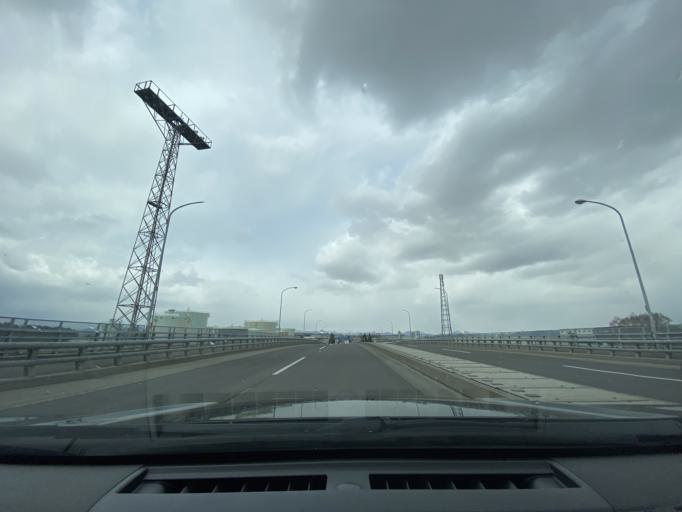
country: JP
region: Hokkaido
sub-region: Asahikawa-shi
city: Asahikawa
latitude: 43.8047
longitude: 142.4188
